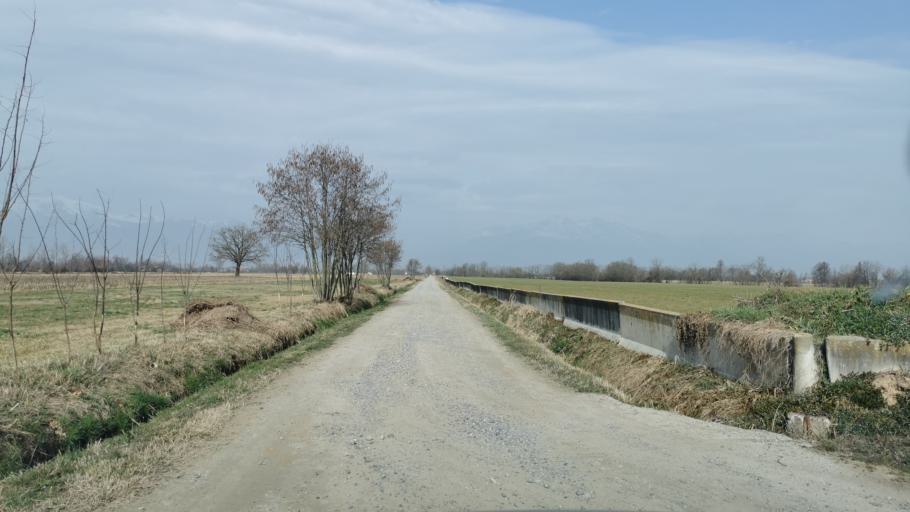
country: IT
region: Piedmont
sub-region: Provincia di Torino
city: Rivarossa
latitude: 45.2735
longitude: 7.7027
